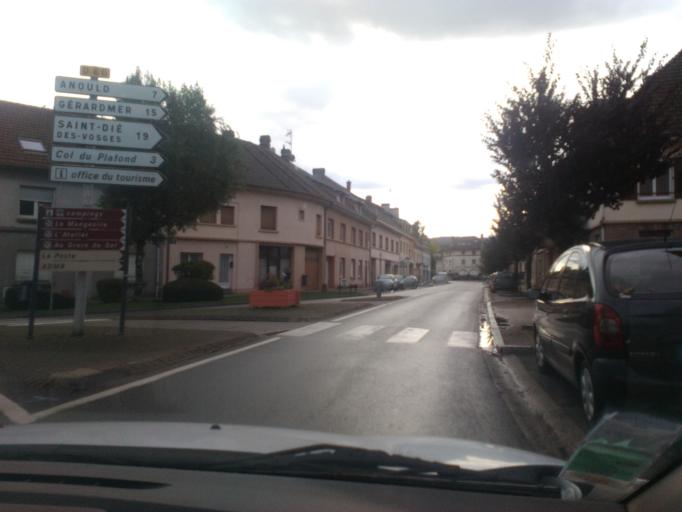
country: FR
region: Lorraine
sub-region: Departement des Vosges
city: Corcieux
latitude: 48.1724
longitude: 6.8805
